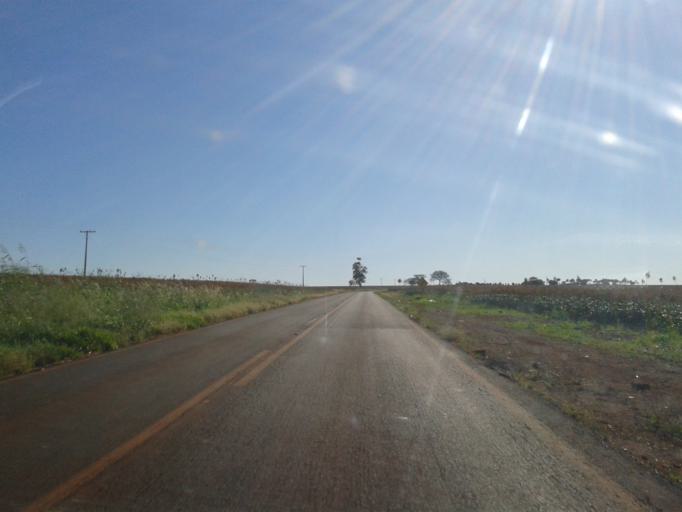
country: BR
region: Minas Gerais
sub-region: Capinopolis
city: Capinopolis
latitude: -18.6672
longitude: -49.5602
